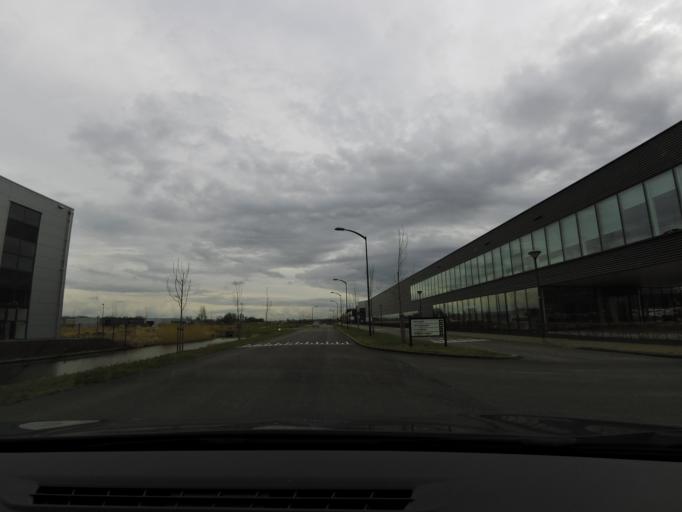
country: NL
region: South Holland
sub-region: Gemeente Waddinxveen
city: Waddinxveen
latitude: 52.0199
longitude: 4.6569
